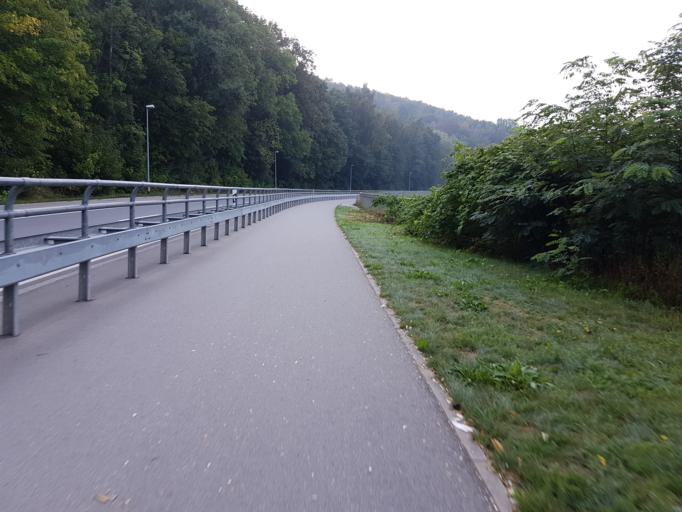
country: DE
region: Saxony
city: Taura
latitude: 50.9222
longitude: 12.8574
